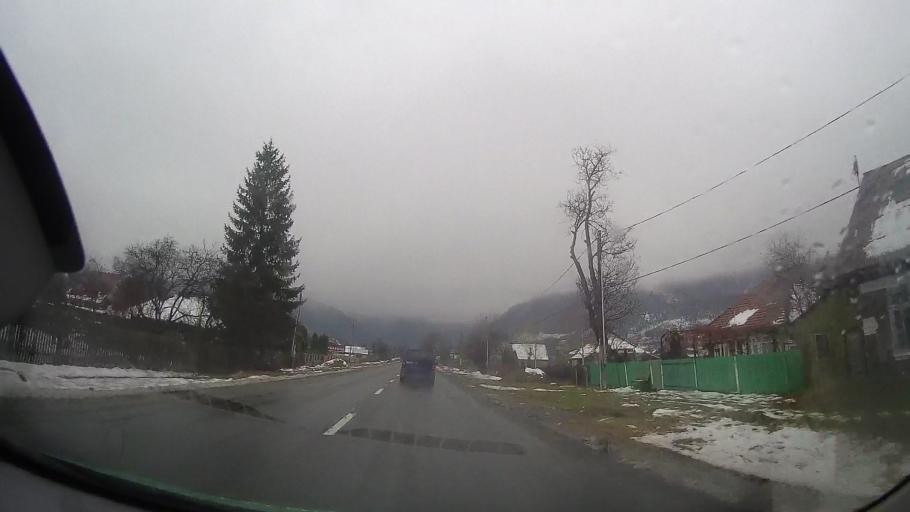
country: RO
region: Neamt
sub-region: Comuna Pangarati
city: Stejaru
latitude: 46.9035
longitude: 26.1748
